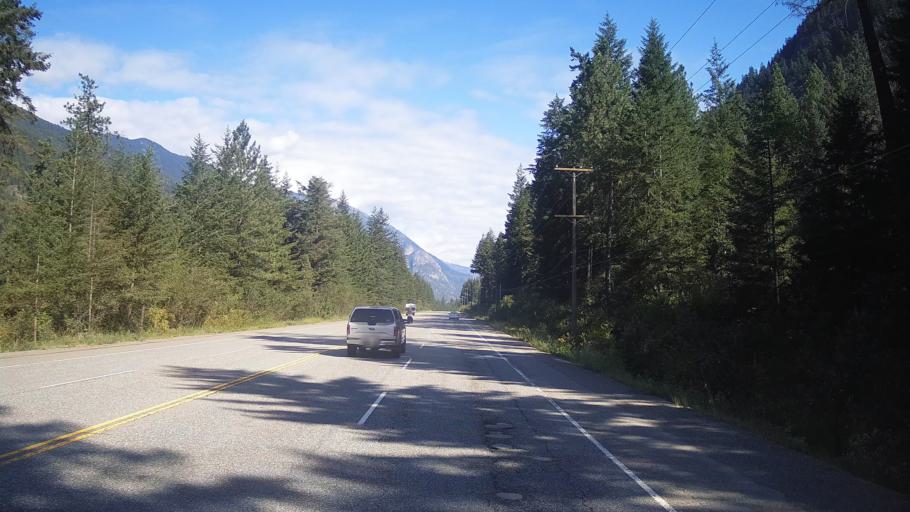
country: CA
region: British Columbia
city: Hope
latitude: 50.0398
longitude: -121.5352
